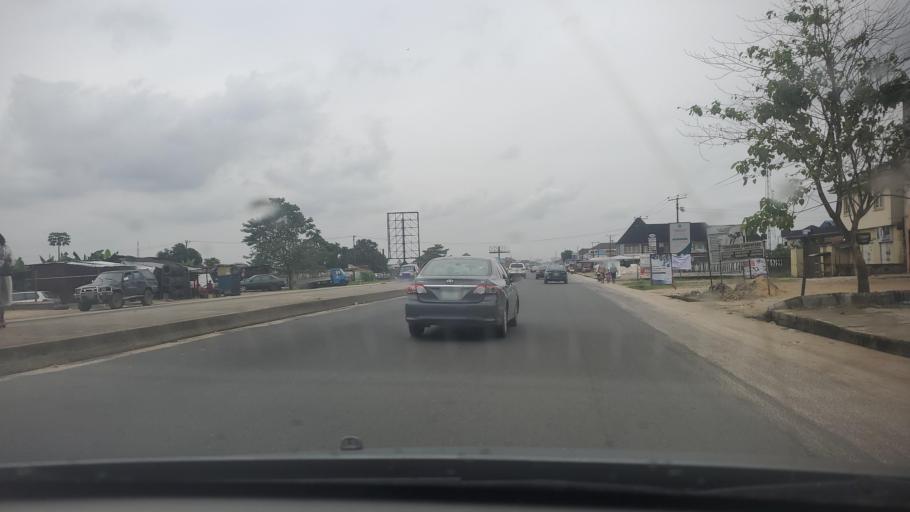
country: NG
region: Rivers
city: Port Harcourt
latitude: 4.8701
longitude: 6.9732
